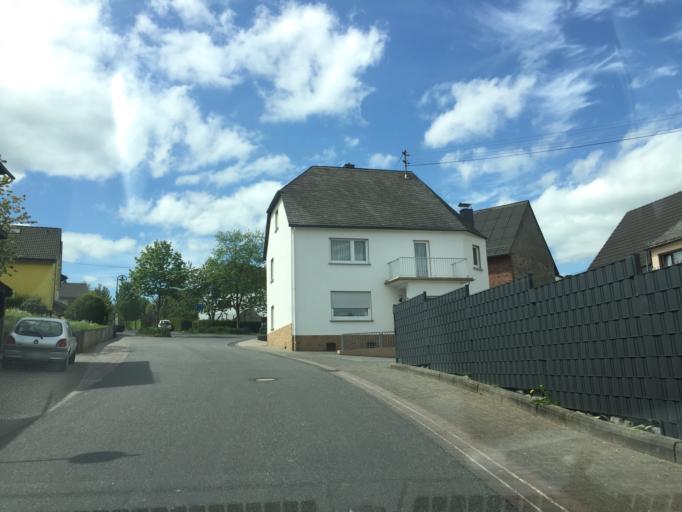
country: DE
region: Rheinland-Pfalz
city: Meudt
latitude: 50.4944
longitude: 7.8956
